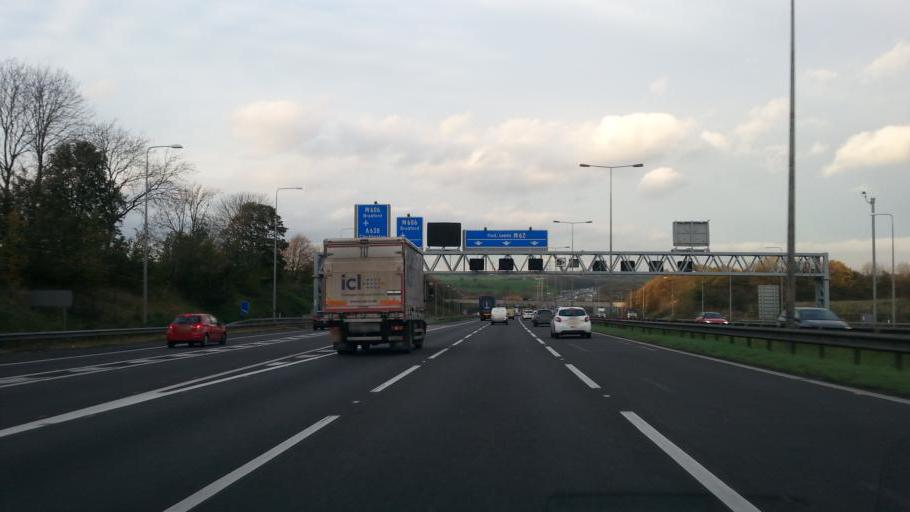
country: GB
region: England
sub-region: Kirklees
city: Cleckheaton
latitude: 53.7301
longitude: -1.7320
